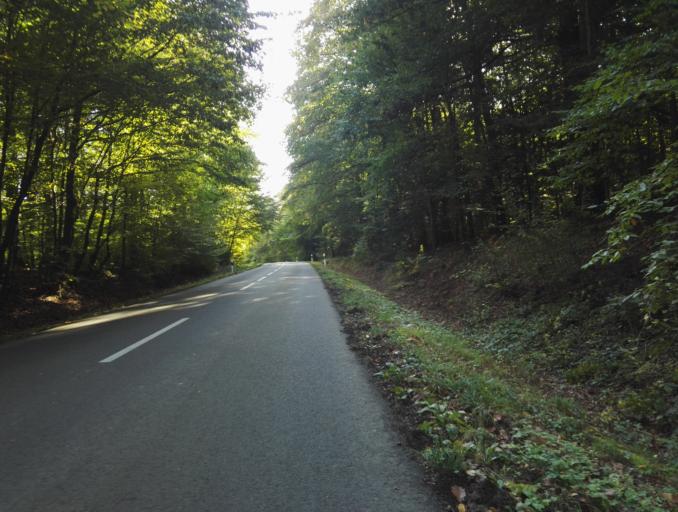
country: DE
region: Lower Saxony
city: Holle
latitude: 52.1345
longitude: 10.1400
